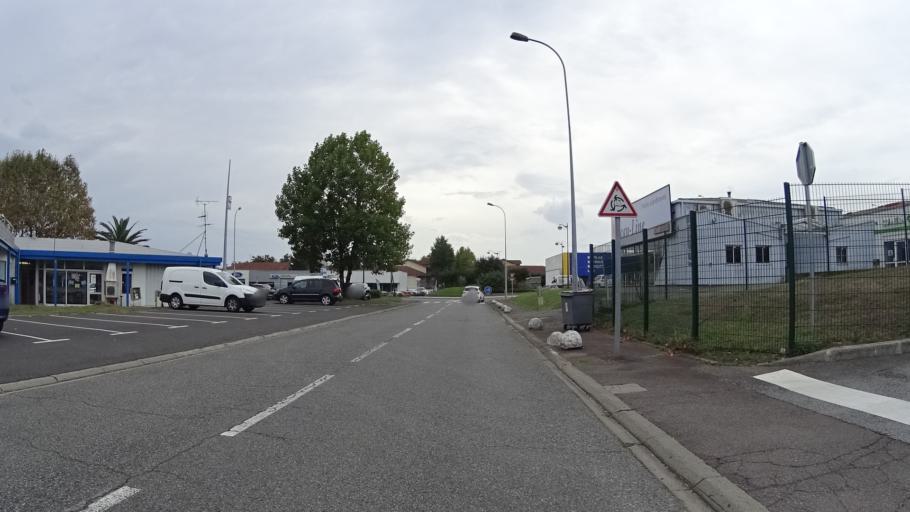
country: FR
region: Aquitaine
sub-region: Departement des Landes
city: Saint-Paul-les-Dax
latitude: 43.7273
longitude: -1.0780
